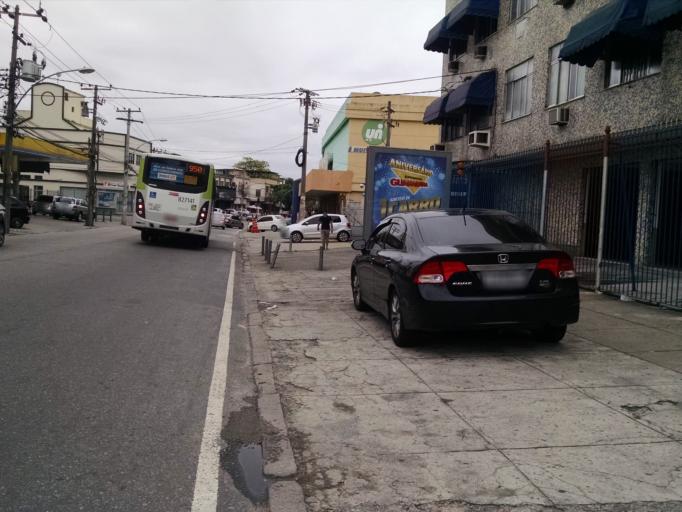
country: BR
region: Rio de Janeiro
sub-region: Duque De Caxias
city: Duque de Caxias
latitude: -22.8354
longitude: -43.3182
